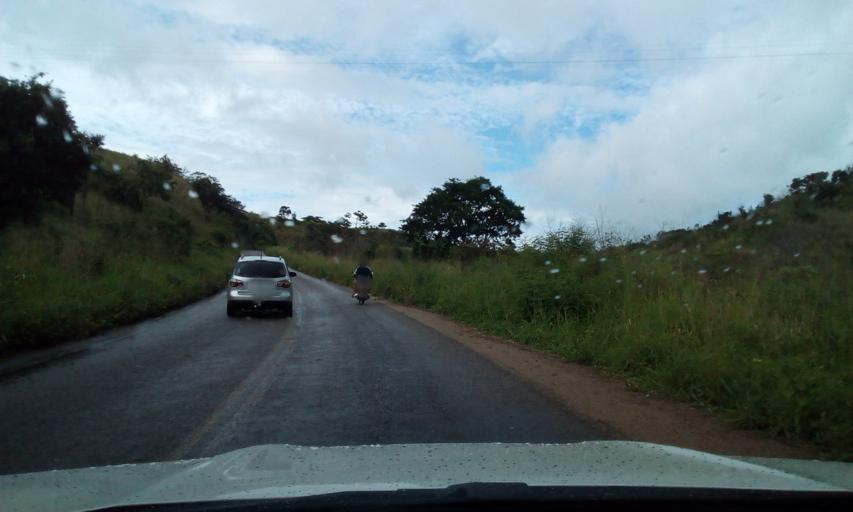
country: BR
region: Paraiba
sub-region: Areia
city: Areia
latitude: -6.9134
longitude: -35.6471
